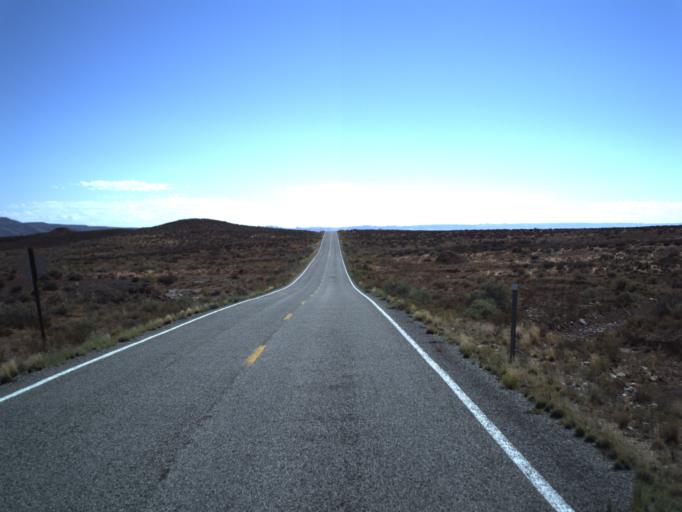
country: US
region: Utah
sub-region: San Juan County
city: Blanding
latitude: 37.2186
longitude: -109.8890
